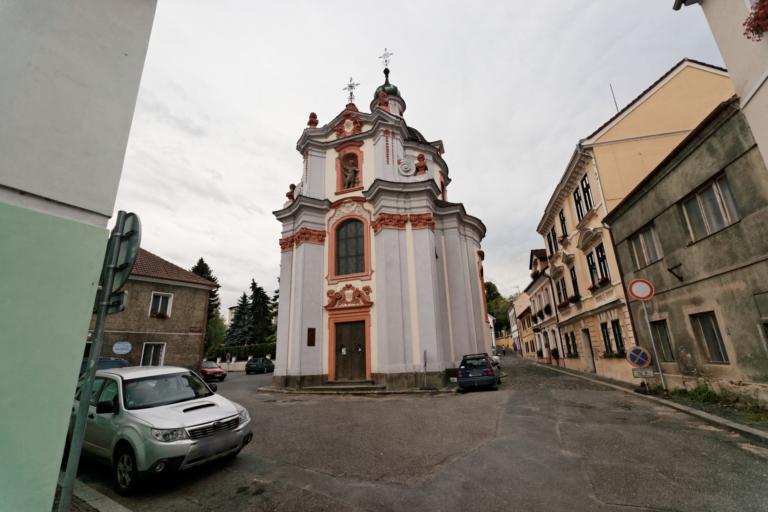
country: CZ
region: Ustecky
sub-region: Okres Litomerice
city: Litomerice
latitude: 50.5335
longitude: 14.1275
